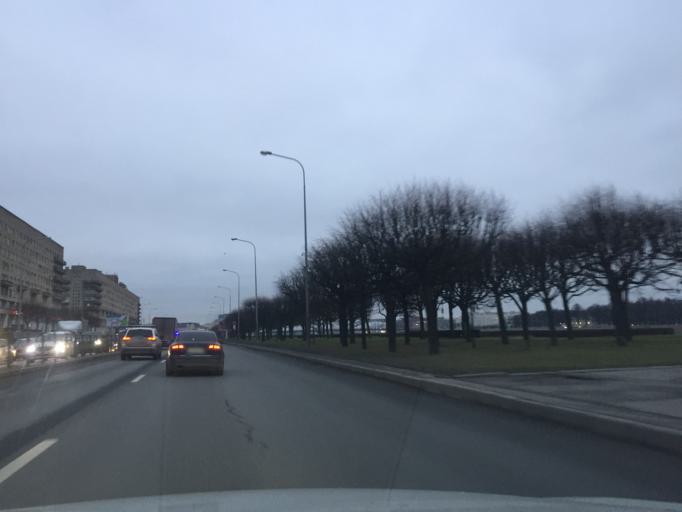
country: RU
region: Leningrad
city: Finlyandskiy
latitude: 59.9533
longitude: 30.4075
